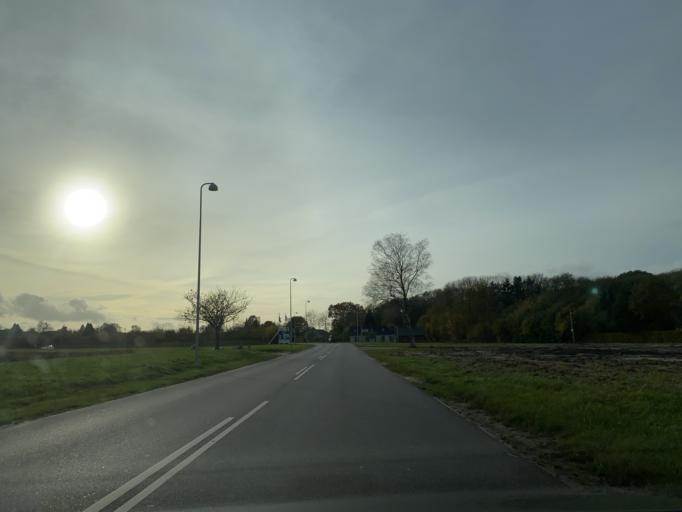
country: DK
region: Central Jutland
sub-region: Skanderborg Kommune
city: Galten
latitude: 56.1613
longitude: 9.9277
